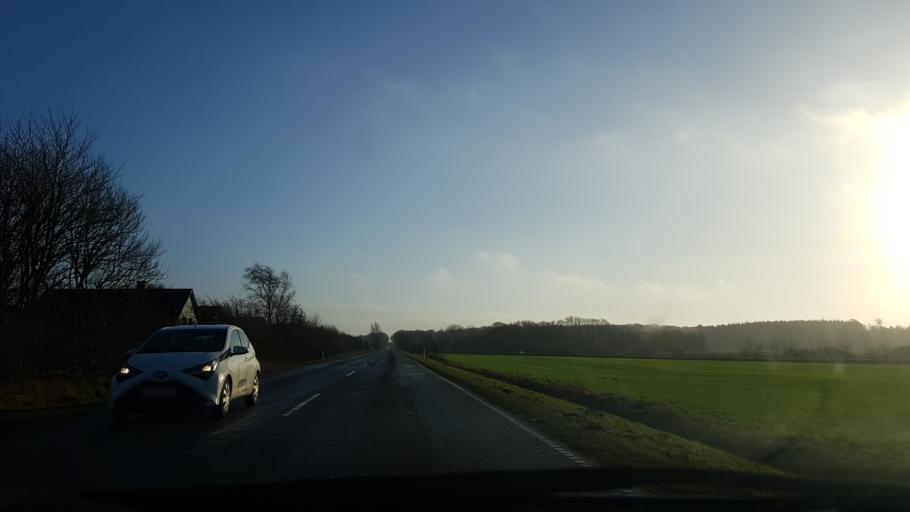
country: DK
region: South Denmark
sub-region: Tonder Kommune
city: Toftlund
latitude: 55.2304
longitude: 9.1694
